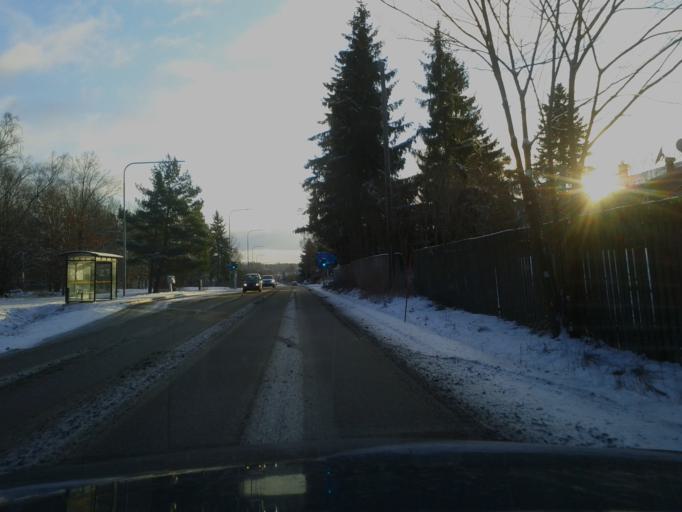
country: SE
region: Stockholm
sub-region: Taby Kommun
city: Taby
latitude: 59.4418
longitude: 18.0333
